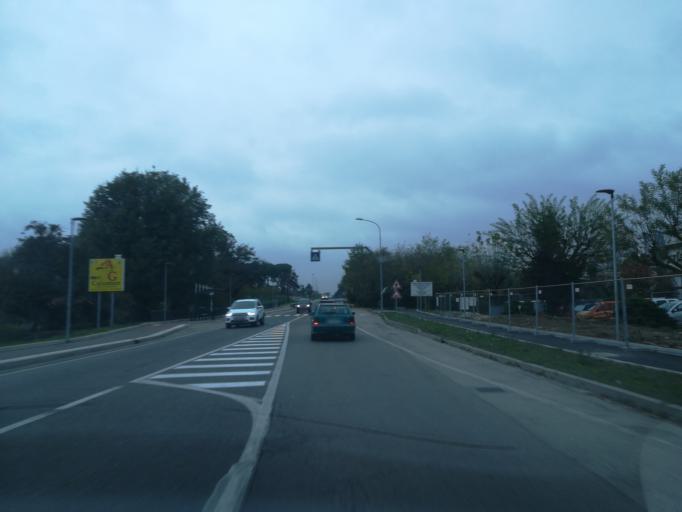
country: IT
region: Emilia-Romagna
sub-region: Provincia di Bologna
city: Toscanella
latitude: 44.3793
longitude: 11.6477
